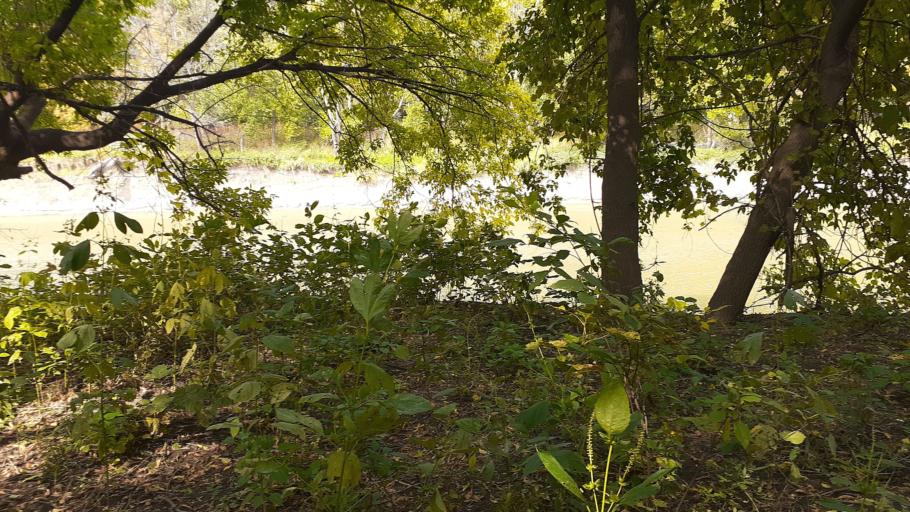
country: US
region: Minnesota
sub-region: Clay County
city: Oakport
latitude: 46.9143
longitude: -96.7614
